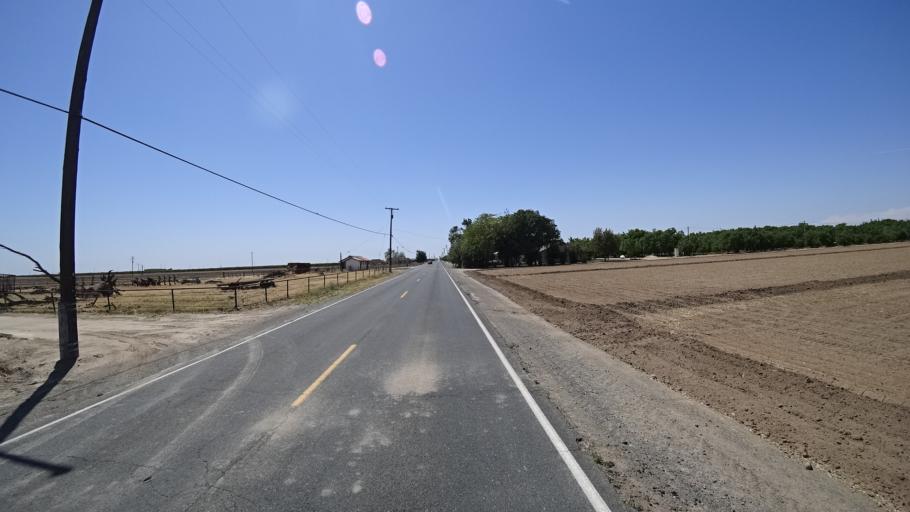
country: US
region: California
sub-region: Kings County
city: Armona
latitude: 36.2482
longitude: -119.7089
